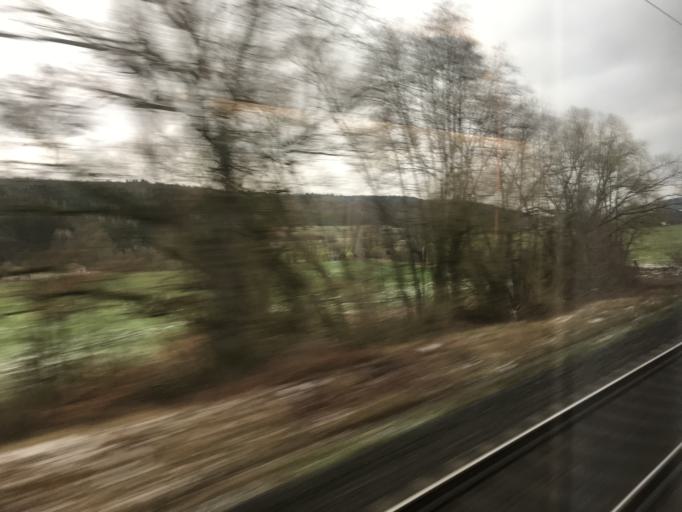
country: DE
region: Hesse
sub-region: Regierungsbezirk Darmstadt
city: Bad Soden-Salmunster
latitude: 50.2652
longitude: 9.3438
